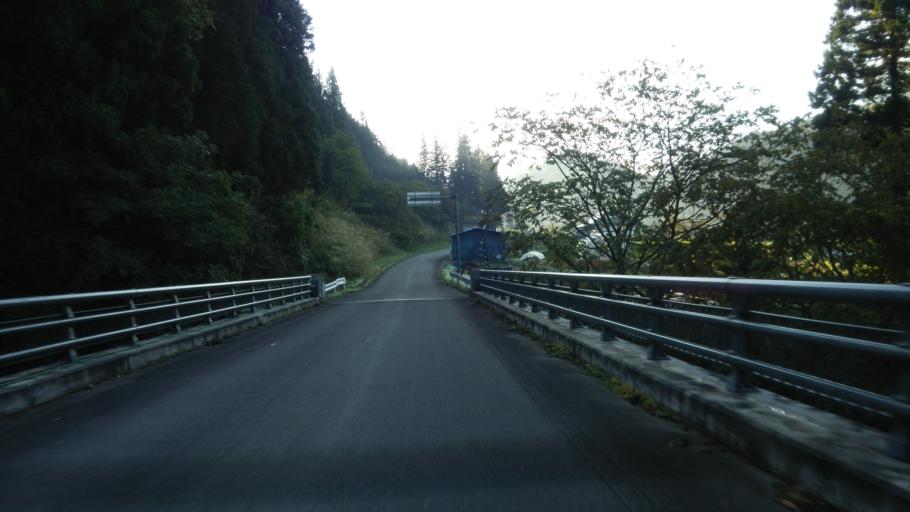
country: JP
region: Fukushima
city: Kitakata
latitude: 37.4439
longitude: 139.7155
